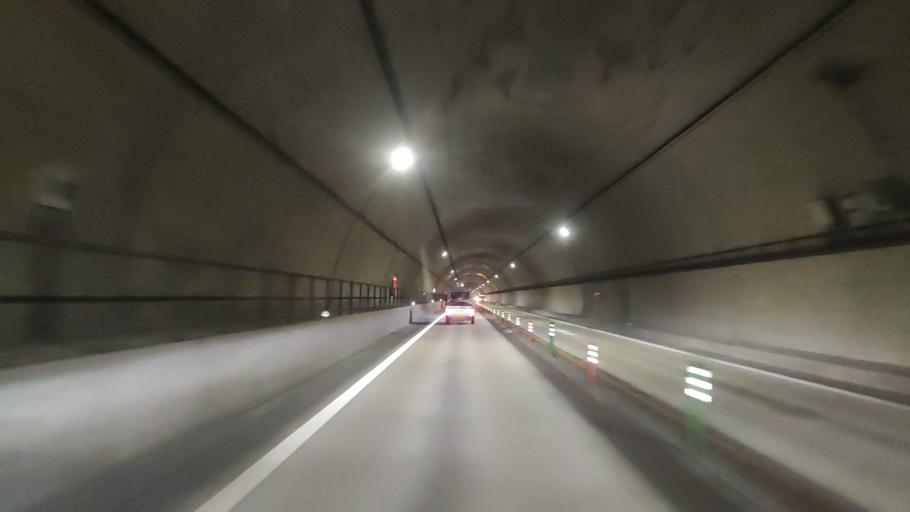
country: JP
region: Wakayama
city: Tanabe
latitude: 33.6200
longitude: 135.4205
